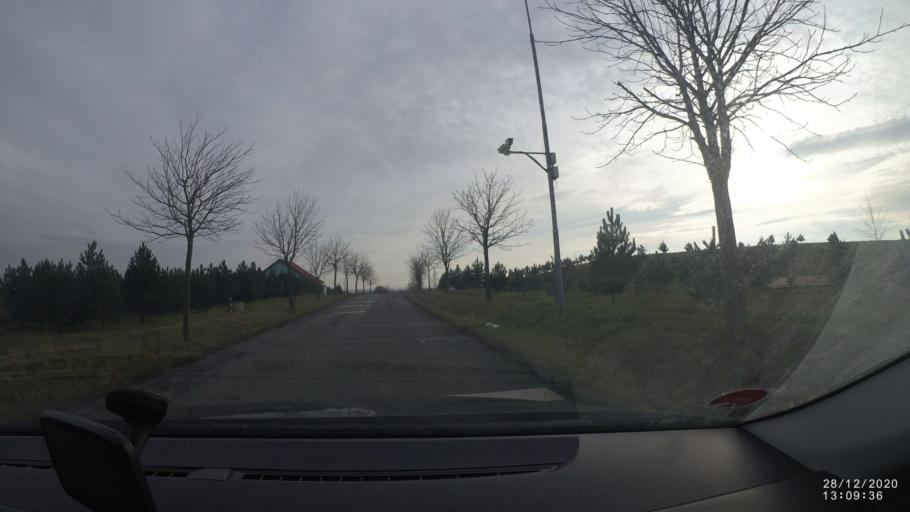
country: CZ
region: Central Bohemia
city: Zelenec
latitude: 50.1262
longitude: 14.6706
